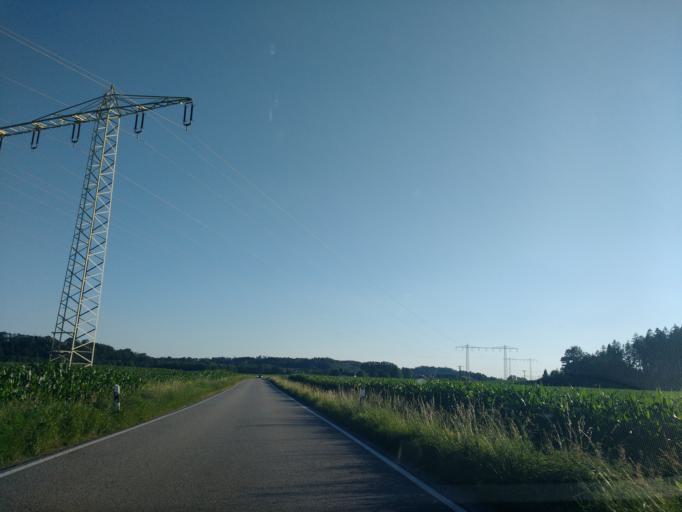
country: DE
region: Bavaria
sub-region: Upper Bavaria
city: Oberneukirchen
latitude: 48.2088
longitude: 12.5014
